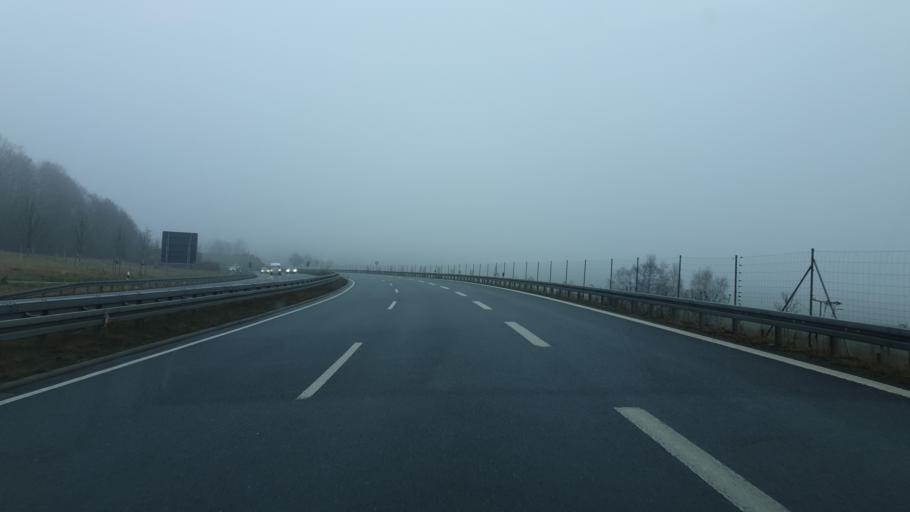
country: DE
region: Saxony
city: Gornau
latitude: 50.7894
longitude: 12.9961
